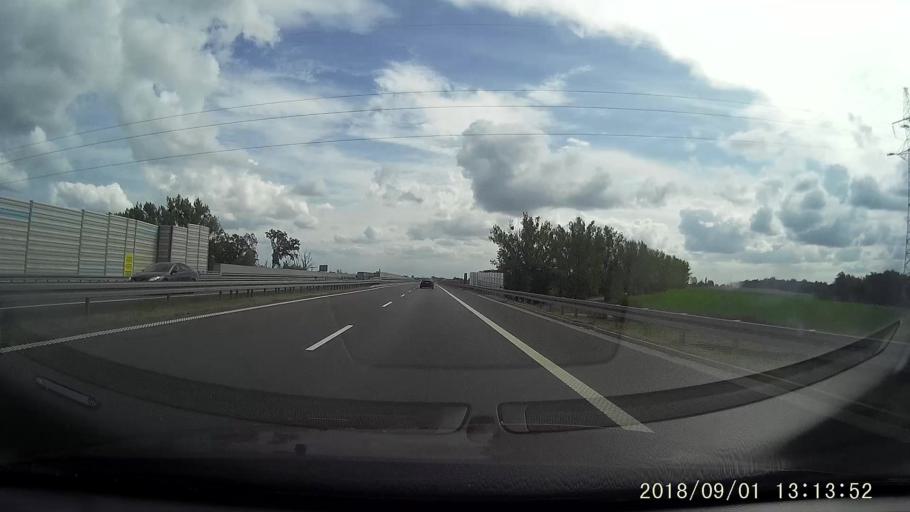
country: PL
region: West Pomeranian Voivodeship
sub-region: Powiat gryfinski
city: Gryfino
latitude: 53.2837
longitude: 14.6102
